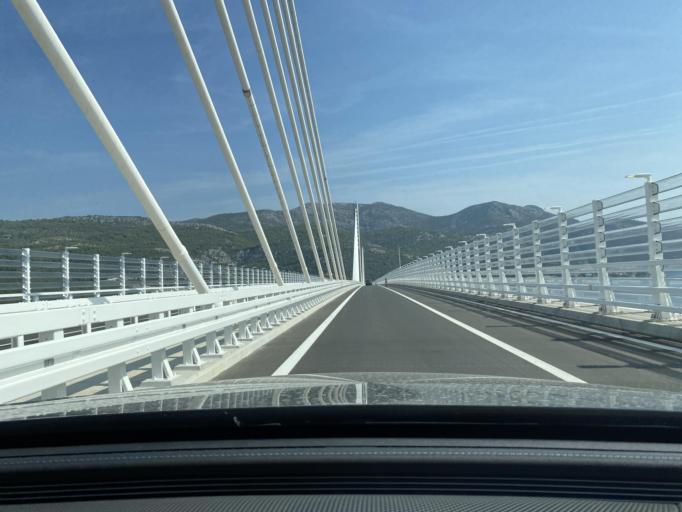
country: BA
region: Federation of Bosnia and Herzegovina
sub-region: Hercegovacko-Bosanski Kanton
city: Neum
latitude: 42.9329
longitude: 17.5372
